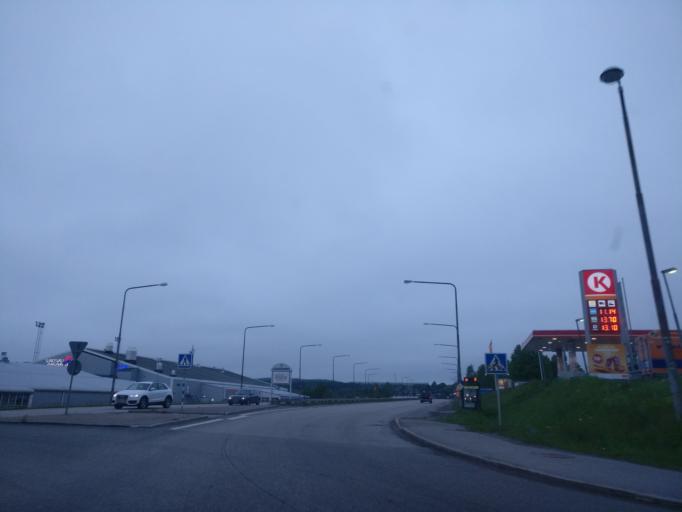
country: SE
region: Vaesternorrland
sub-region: Sundsvalls Kommun
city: Johannedal
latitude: 62.4133
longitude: 17.3497
